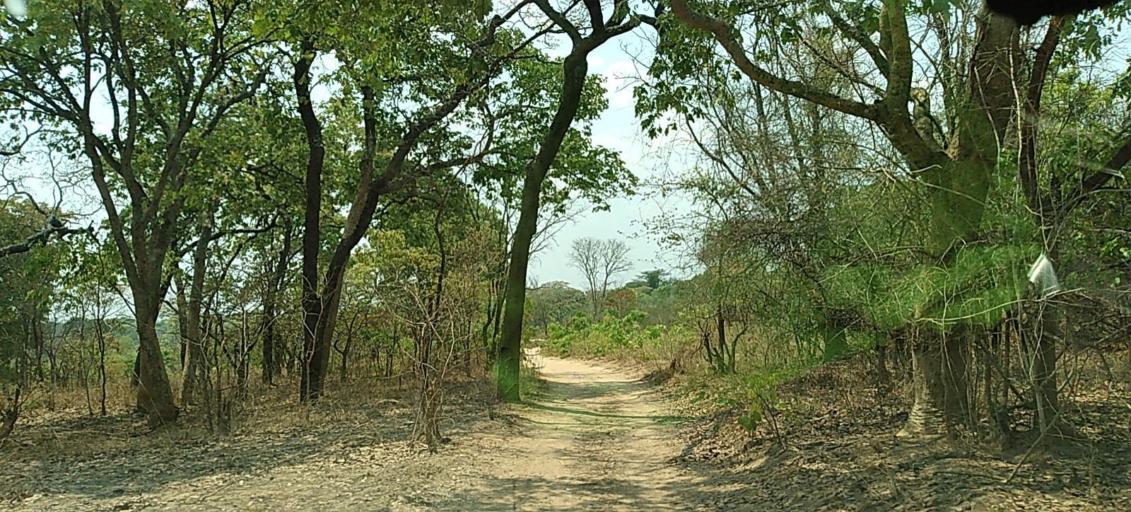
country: ZM
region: North-Western
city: Kabompo
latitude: -13.6529
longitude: 24.3737
